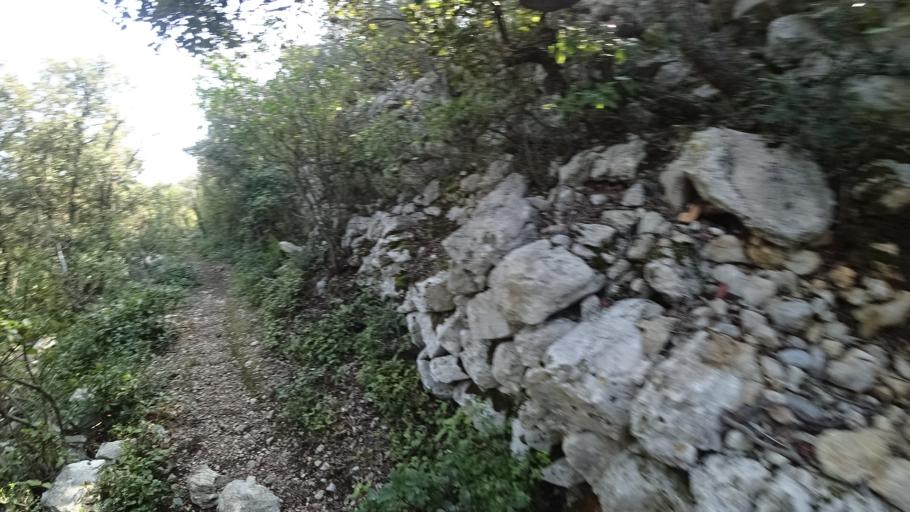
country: HR
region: Primorsko-Goranska
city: Mali Losinj
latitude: 44.4950
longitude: 14.5293
